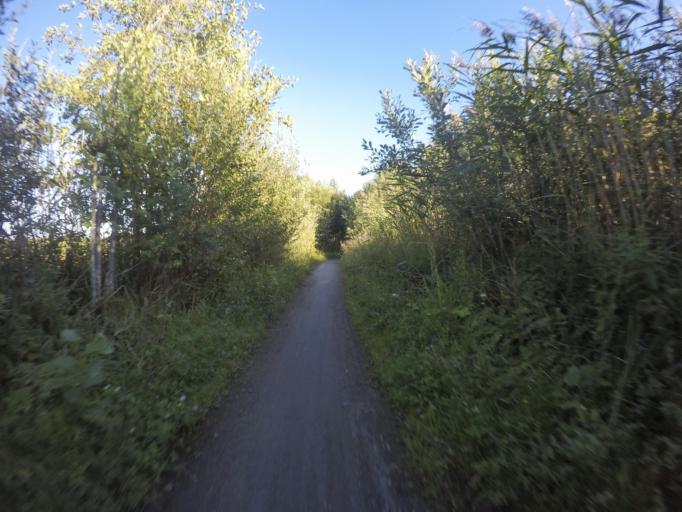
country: SE
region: Vaestmanland
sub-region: Vasteras
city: Vasteras
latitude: 59.5734
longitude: 16.6390
